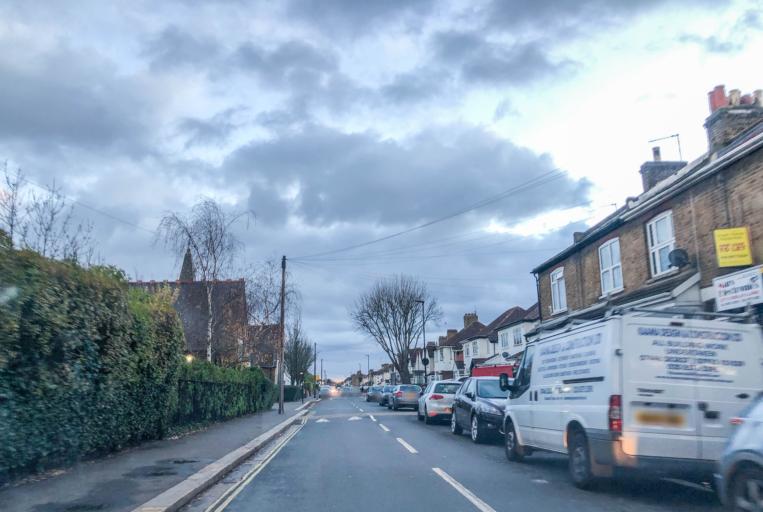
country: GB
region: England
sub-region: Greater London
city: Hounslow
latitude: 51.4650
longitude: -0.3737
